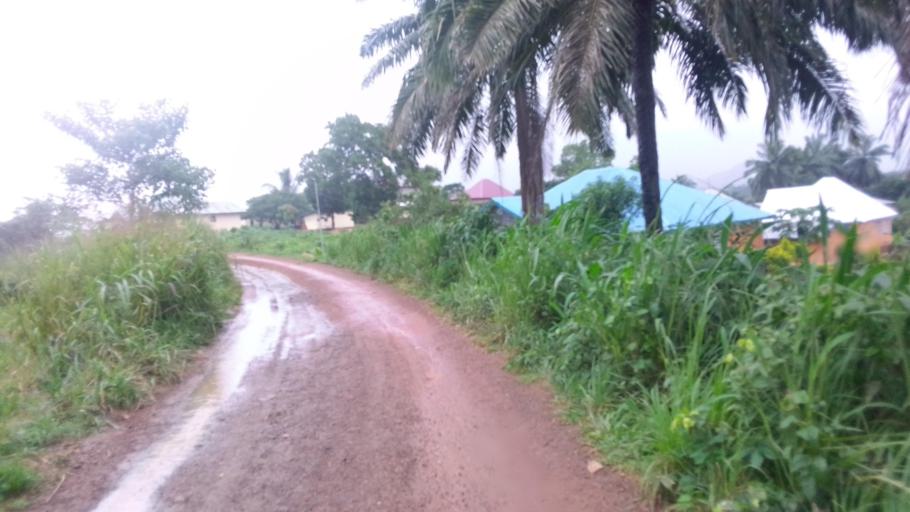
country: SL
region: Eastern Province
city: Kenema
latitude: 7.9029
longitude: -11.1658
